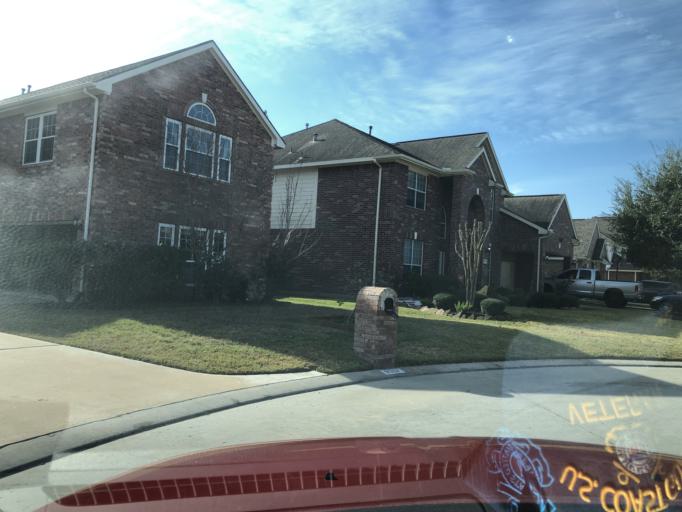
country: US
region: Texas
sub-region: Harris County
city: Tomball
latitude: 30.0245
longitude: -95.5603
